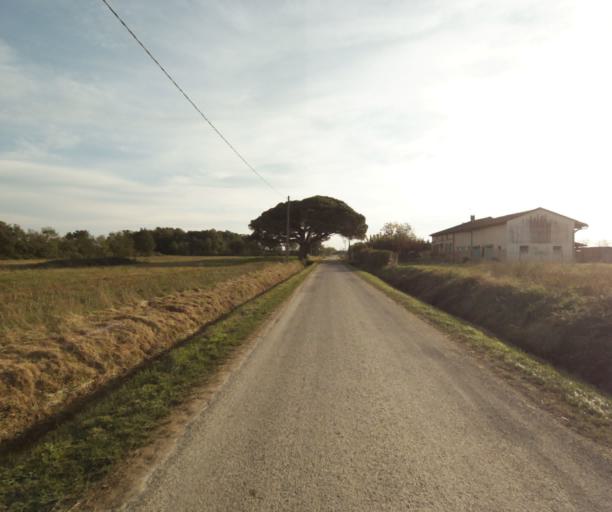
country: FR
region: Midi-Pyrenees
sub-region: Departement du Tarn-et-Garonne
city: Labastide-Saint-Pierre
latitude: 43.8942
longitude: 1.3573
